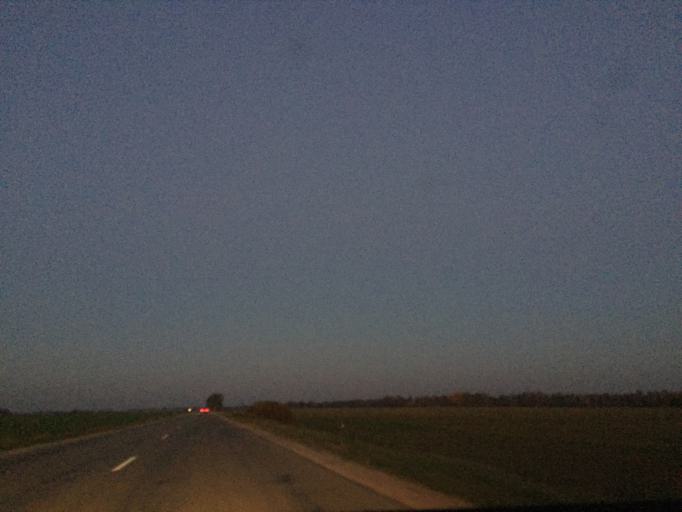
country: LV
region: Tervete
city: Zelmeni
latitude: 56.4921
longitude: 23.2268
